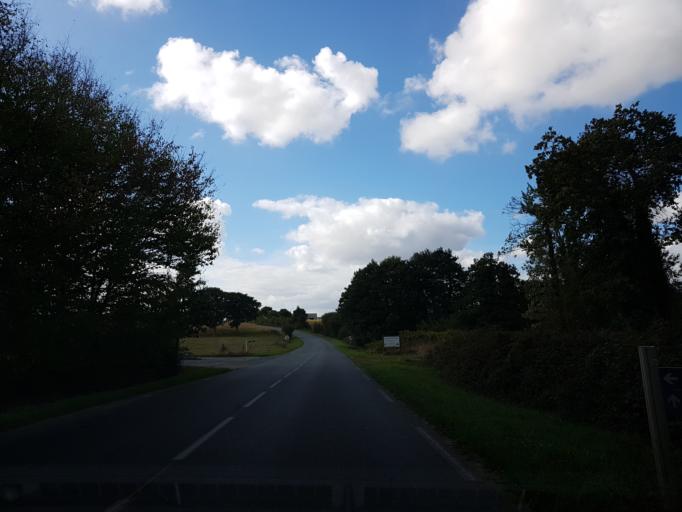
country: FR
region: Brittany
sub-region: Departement des Cotes-d'Armor
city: Langueux
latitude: 48.4646
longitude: -2.7043
